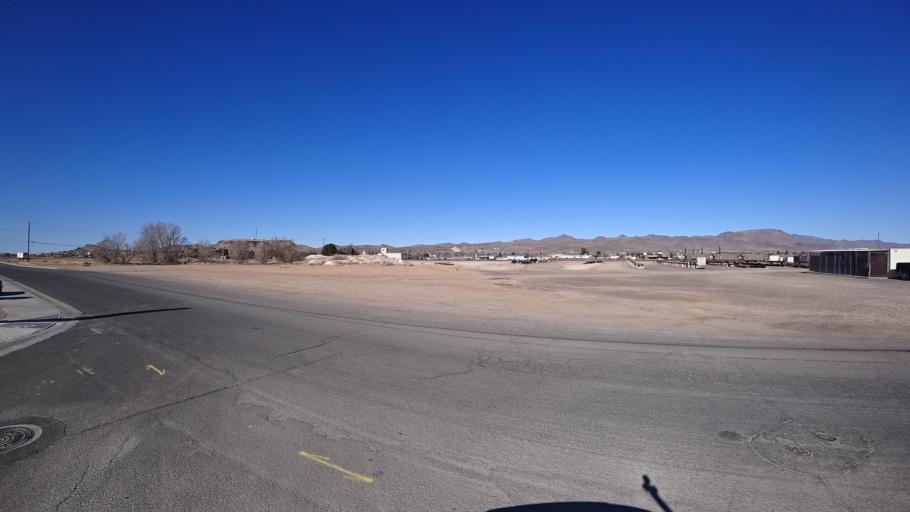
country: US
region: Arizona
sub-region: Mohave County
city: Kingman
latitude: 35.2035
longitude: -114.0217
